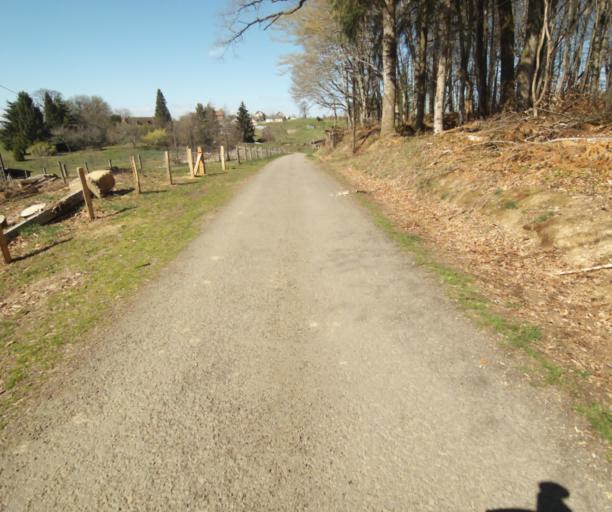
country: FR
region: Limousin
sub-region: Departement de la Correze
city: Saint-Mexant
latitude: 45.3020
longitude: 1.6711
